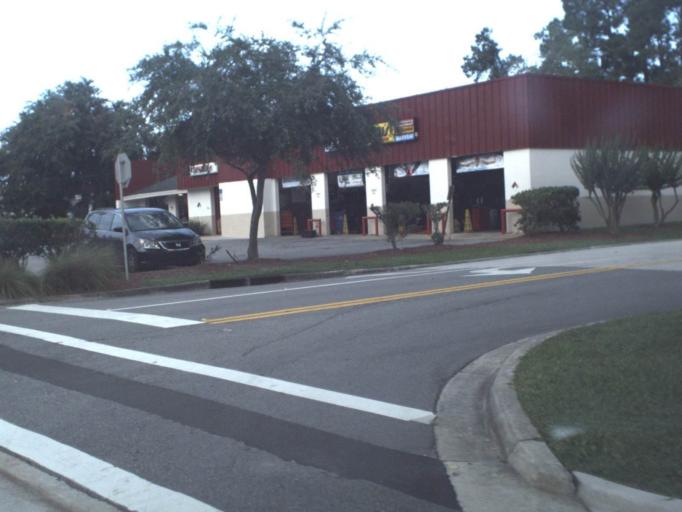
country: US
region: Florida
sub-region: Clay County
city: Orange Park
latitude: 30.2076
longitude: -81.6174
